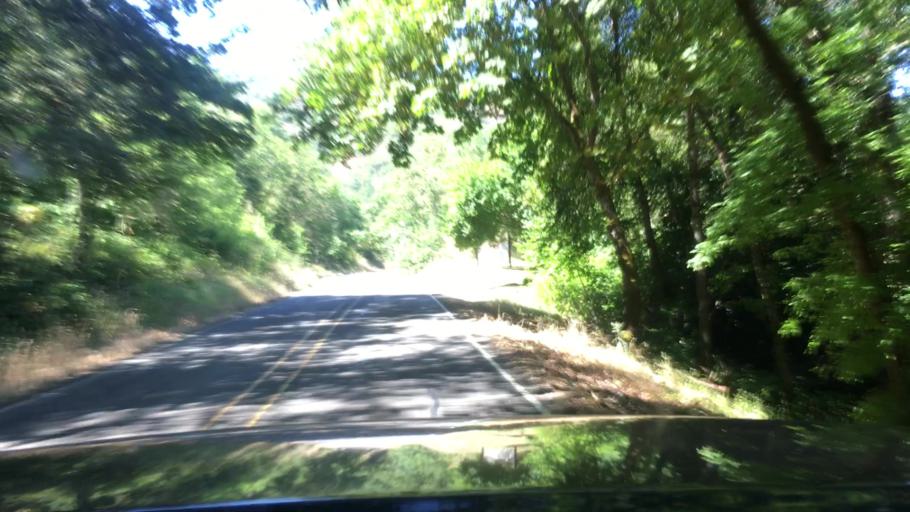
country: US
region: Oregon
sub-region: Douglas County
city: Winston
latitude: 43.1405
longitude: -123.4140
